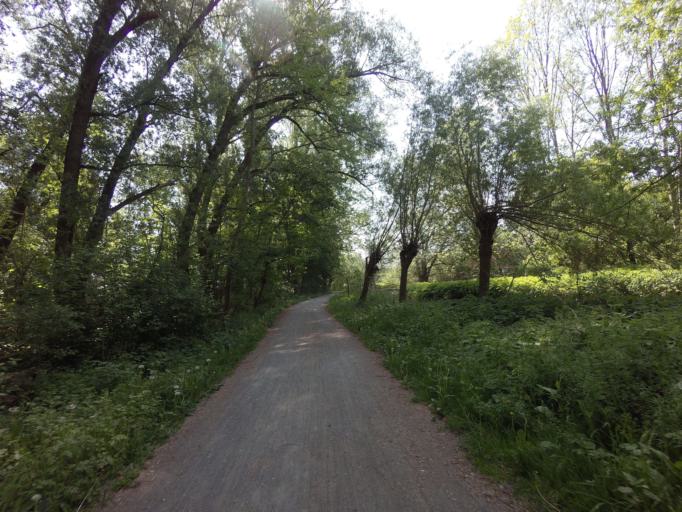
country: DE
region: Lower Saxony
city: Braunschweig
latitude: 52.2729
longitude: 10.5632
